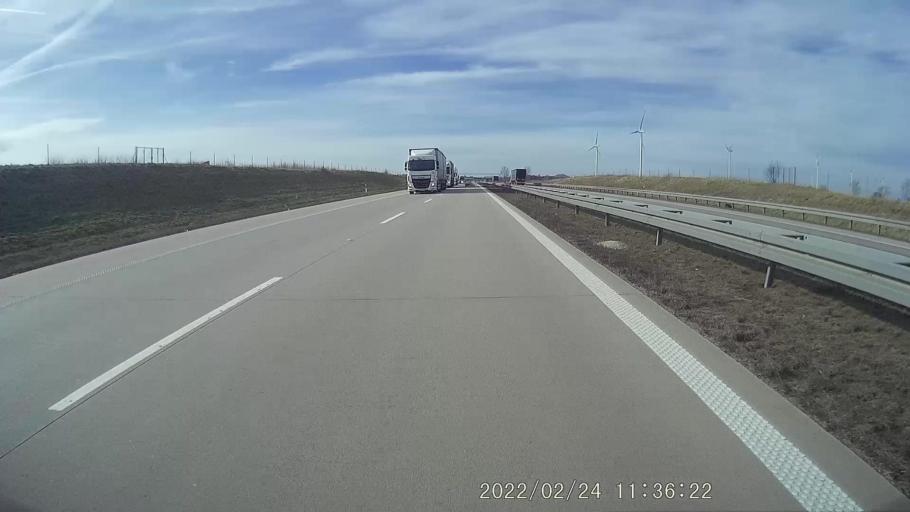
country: PL
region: Lower Silesian Voivodeship
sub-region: Powiat polkowicki
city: Przemkow
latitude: 51.5226
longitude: 15.8056
